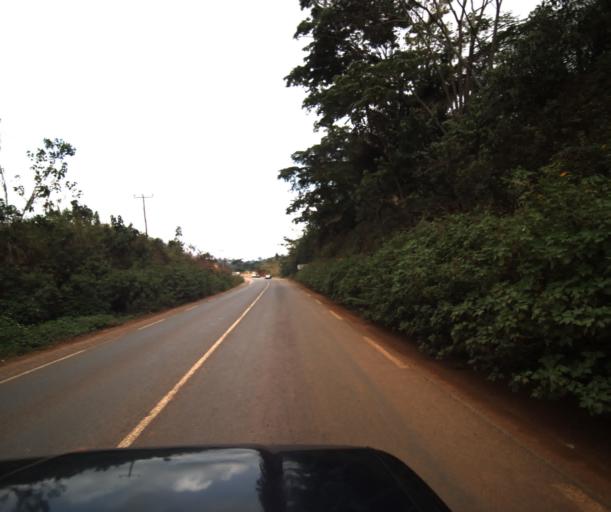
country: CM
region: Centre
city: Mbankomo
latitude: 3.7882
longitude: 11.4447
